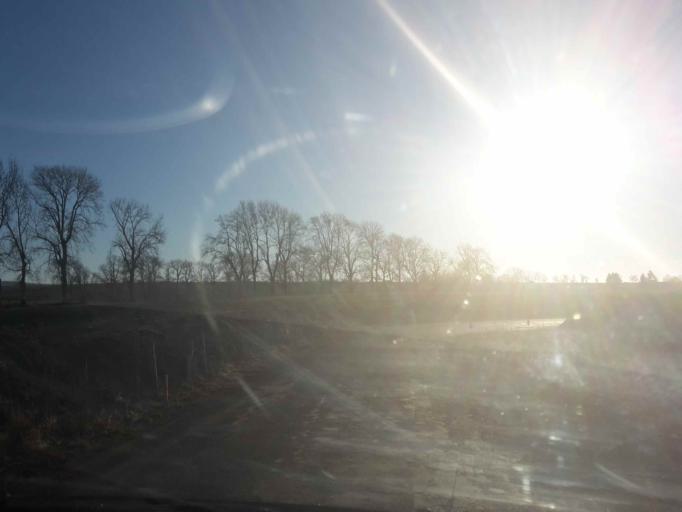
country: FR
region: Auvergne
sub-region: Departement du Cantal
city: Riom-es-Montagnes
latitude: 45.2624
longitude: 2.5616
